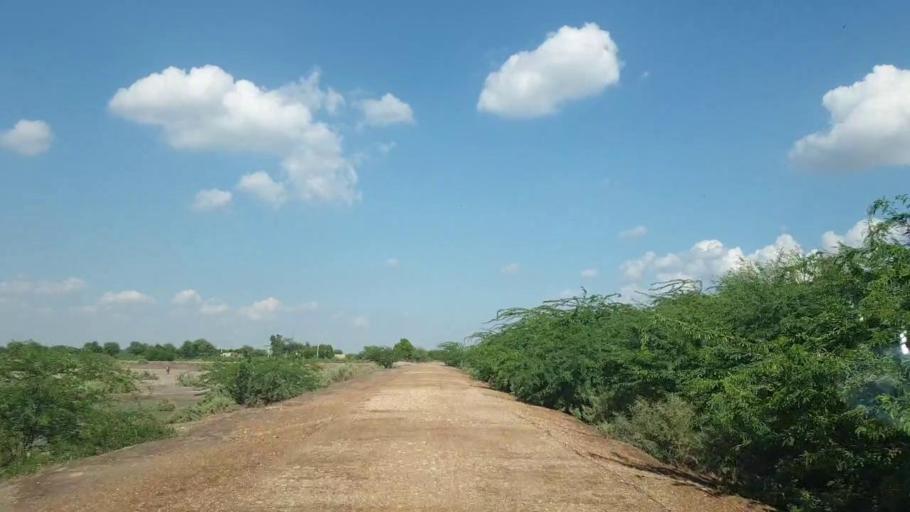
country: PK
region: Sindh
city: Pithoro
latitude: 25.5983
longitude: 69.4018
